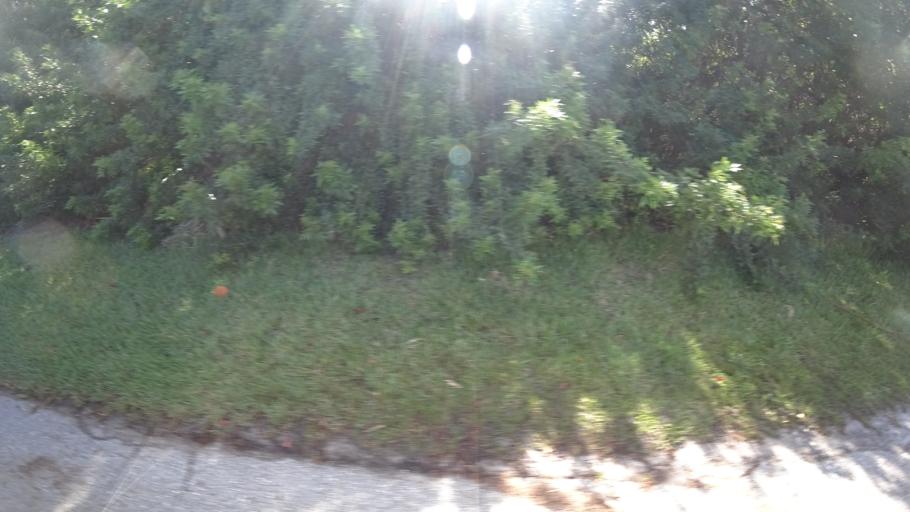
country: US
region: Florida
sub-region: Manatee County
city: West Bradenton
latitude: 27.5030
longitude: -82.6448
